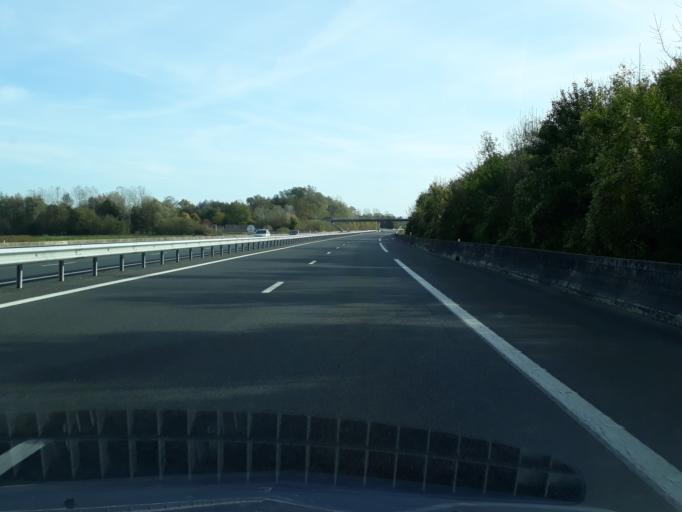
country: FR
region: Champagne-Ardenne
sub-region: Departement de l'Aube
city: Bucheres
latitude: 48.2224
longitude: 4.1193
